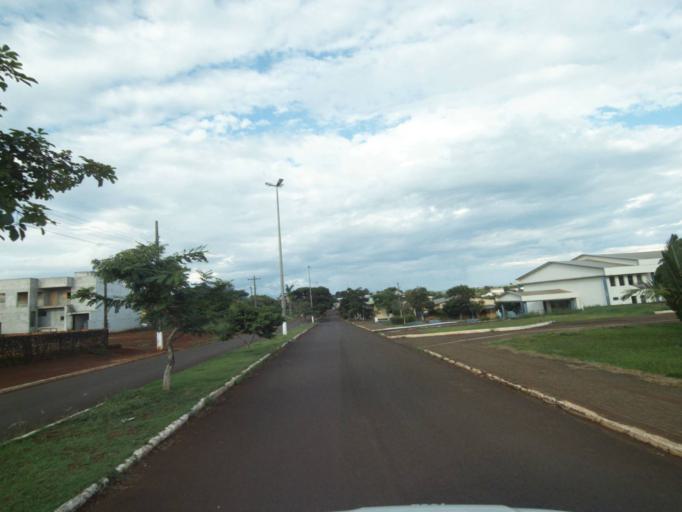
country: BR
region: Parana
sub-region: Laranjeiras Do Sul
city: Laranjeiras do Sul
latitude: -25.4946
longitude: -52.5329
